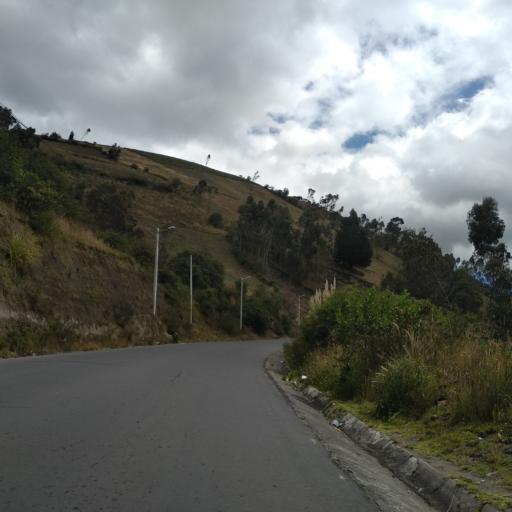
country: EC
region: Cotopaxi
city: Saquisili
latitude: -0.7521
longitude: -78.7254
